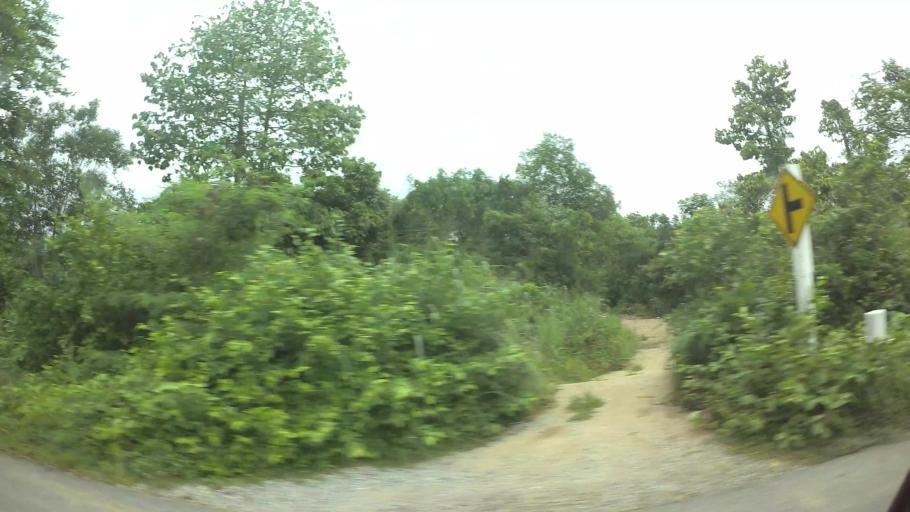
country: TH
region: Chon Buri
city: Si Racha
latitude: 13.1840
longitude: 100.9751
